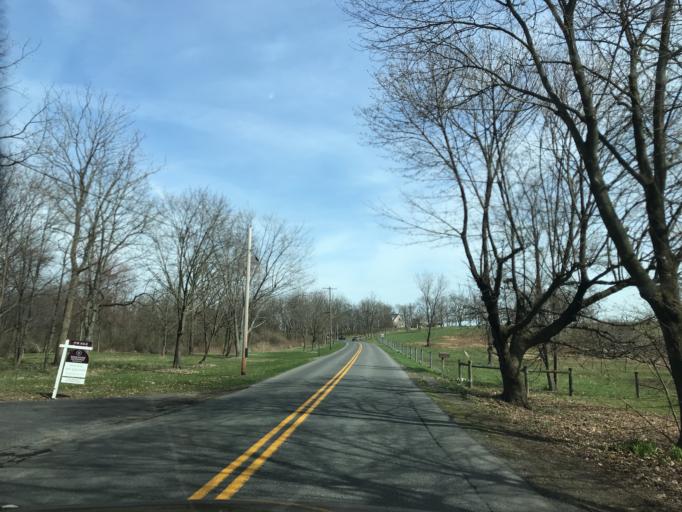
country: US
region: Pennsylvania
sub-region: Northumberland County
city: Northumberland
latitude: 40.8885
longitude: -76.8320
